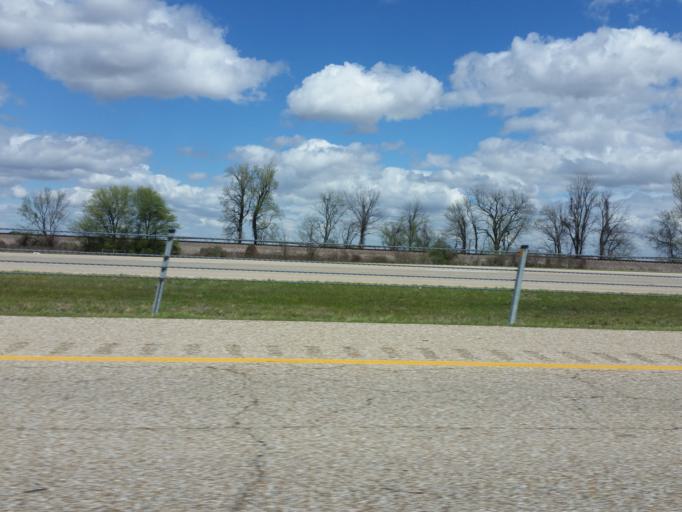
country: US
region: Arkansas
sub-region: Poinsett County
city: Marked Tree
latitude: 35.4707
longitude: -90.3295
